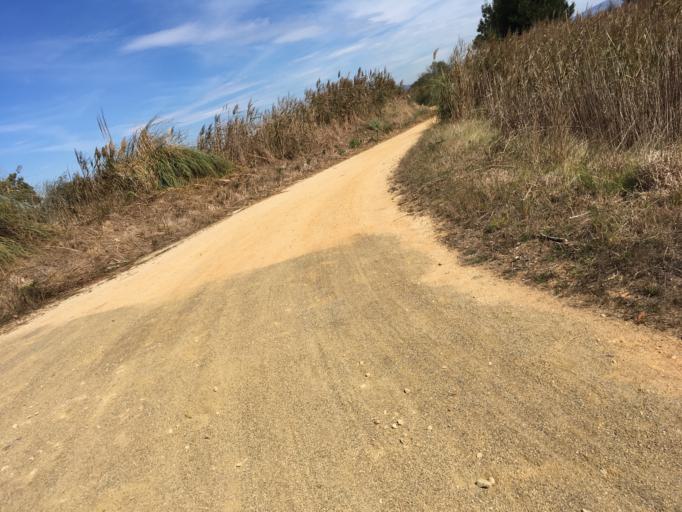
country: PT
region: Aveiro
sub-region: Murtosa
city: Murtosa
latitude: 40.7289
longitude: -8.6030
